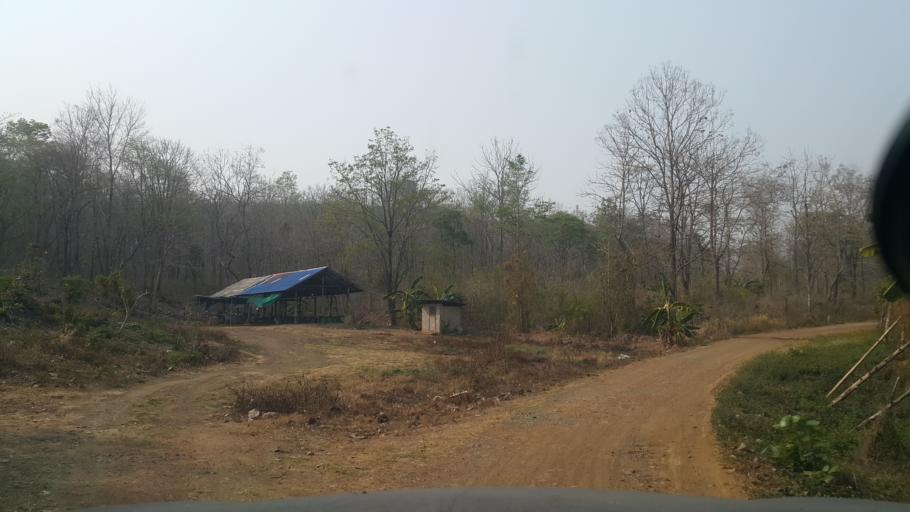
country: TH
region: Chiang Mai
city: Mae On
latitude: 18.7708
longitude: 99.2692
